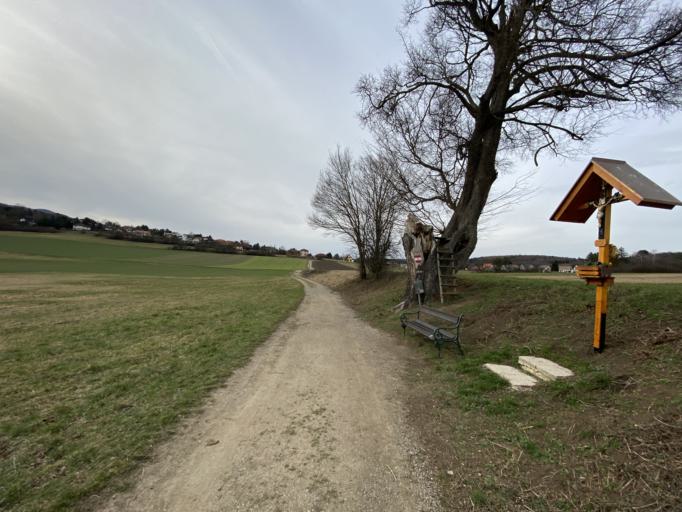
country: AT
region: Lower Austria
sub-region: Politischer Bezirk Modling
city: Gaaden
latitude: 48.0366
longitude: 16.1854
